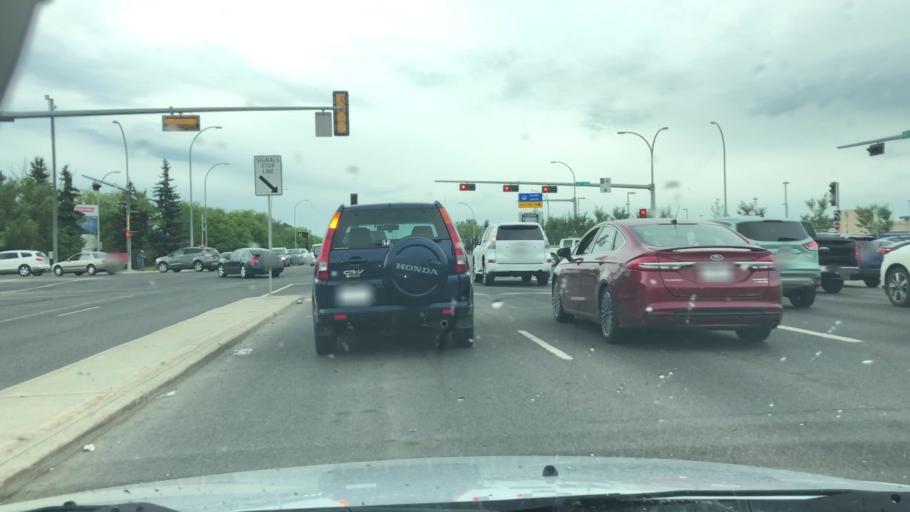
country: CA
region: Alberta
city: Edmonton
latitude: 53.5990
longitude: -113.4920
